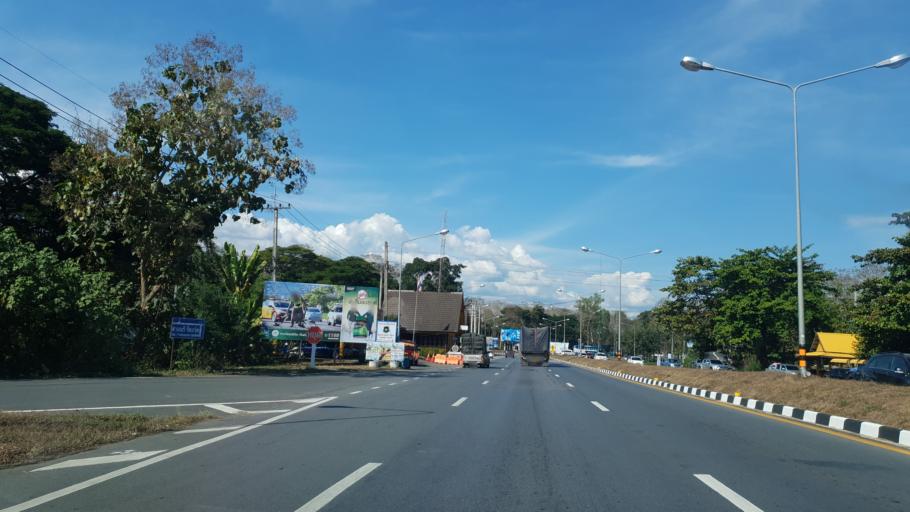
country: TH
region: Phrae
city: Den Chai
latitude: 17.9667
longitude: 100.0660
